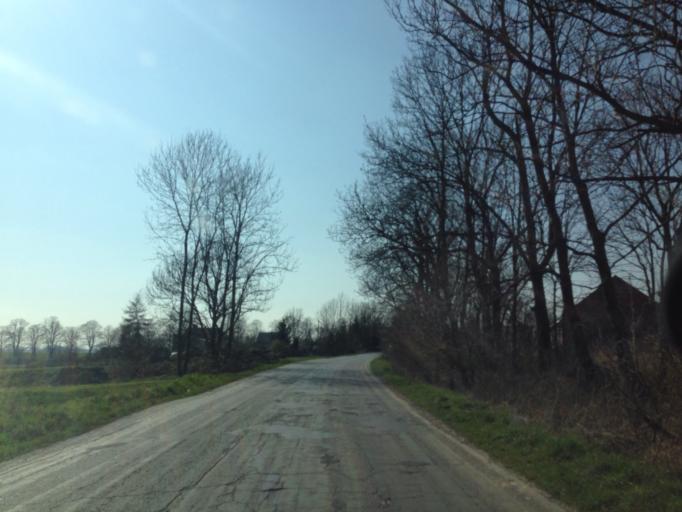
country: PL
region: Lower Silesian Voivodeship
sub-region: Powiat olesnicki
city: Bierutow
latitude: 51.1921
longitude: 17.5110
